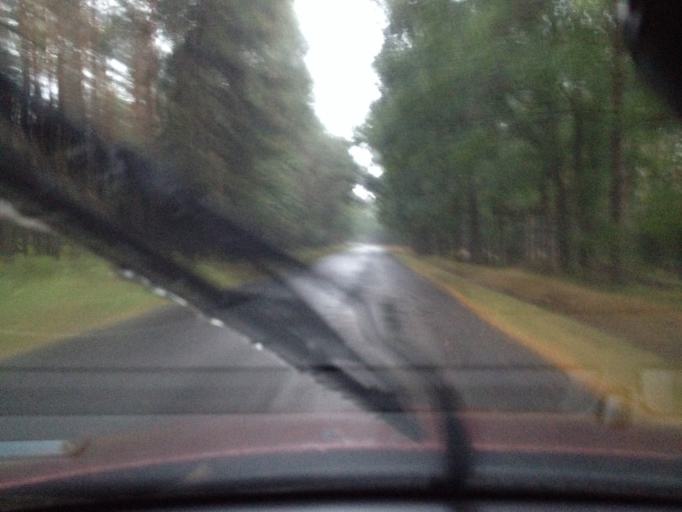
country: PL
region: Lubusz
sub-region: Powiat zaganski
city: Gozdnica
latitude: 51.3416
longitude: 15.1064
